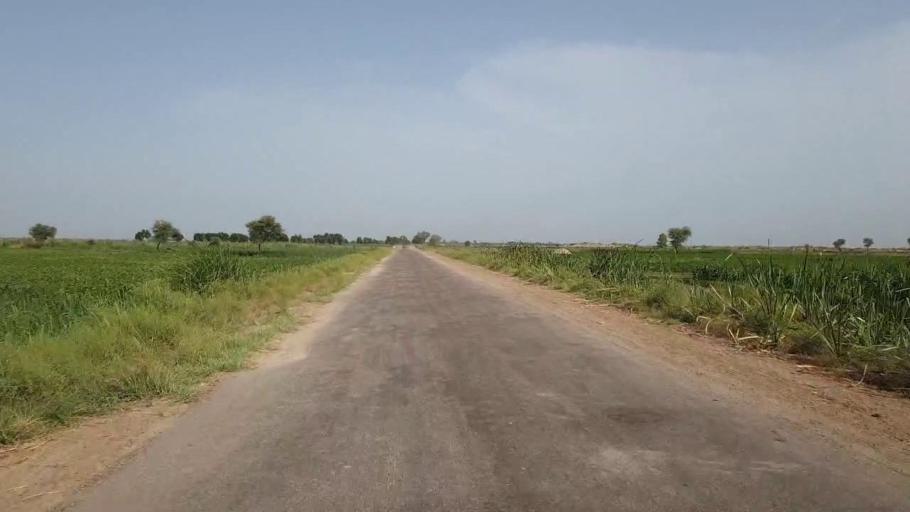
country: PK
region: Sindh
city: Sakrand
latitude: 26.2824
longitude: 68.2656
